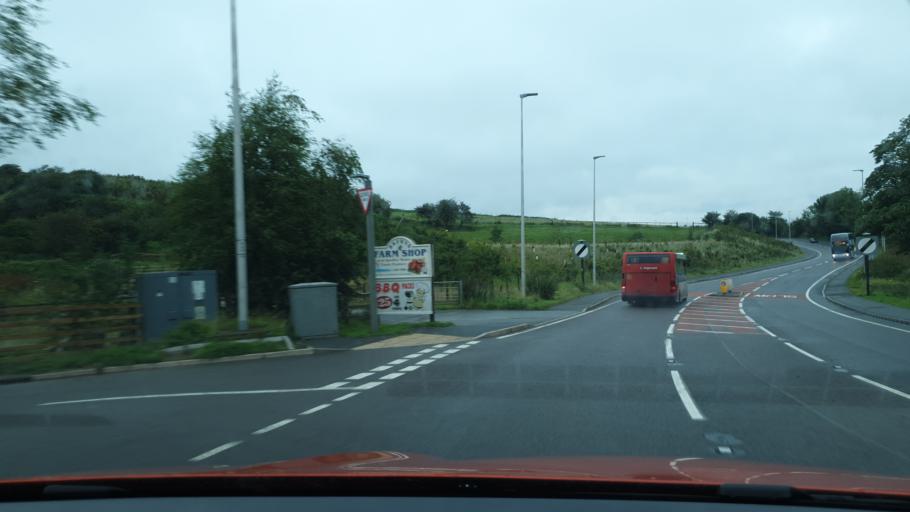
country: GB
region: England
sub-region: Cumbria
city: Dalton in Furness
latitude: 54.1749
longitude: -3.1406
